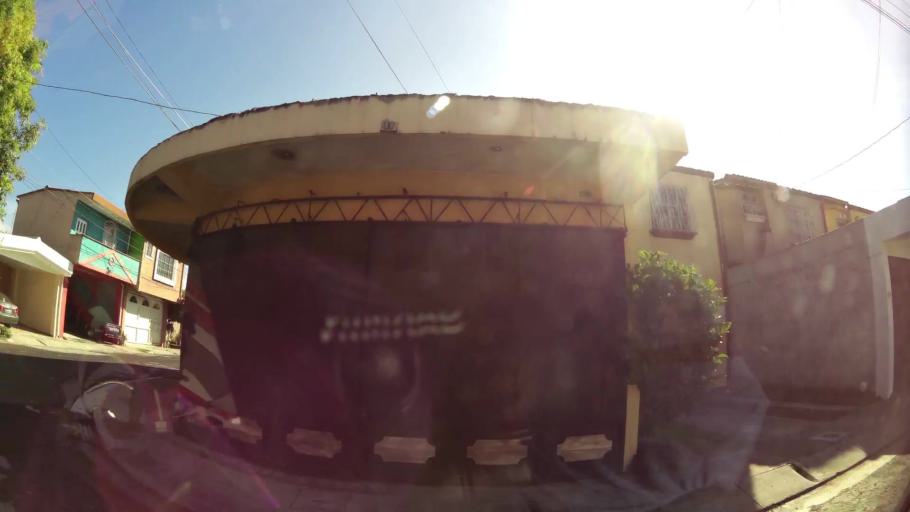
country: SV
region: La Libertad
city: Santa Tecla
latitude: 13.6791
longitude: -89.2997
